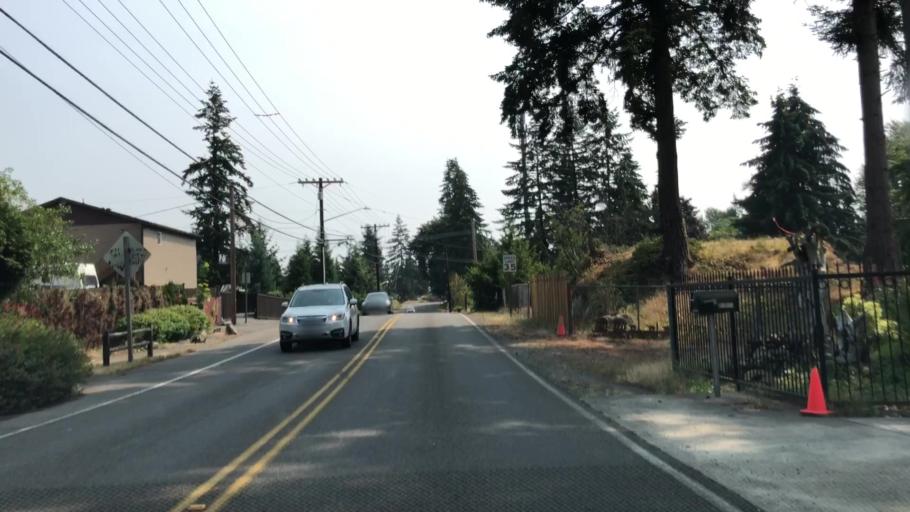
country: US
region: Washington
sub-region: Snohomish County
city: Brier
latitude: 47.8077
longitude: -122.2541
